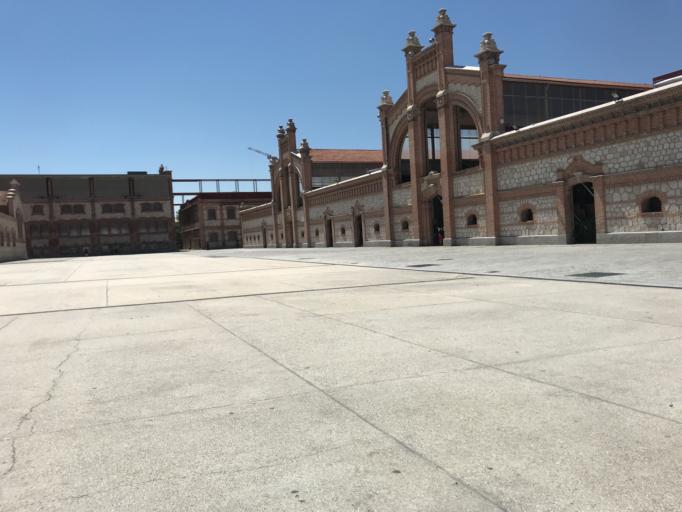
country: ES
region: Madrid
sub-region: Provincia de Madrid
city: Usera
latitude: 40.3916
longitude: -3.6983
